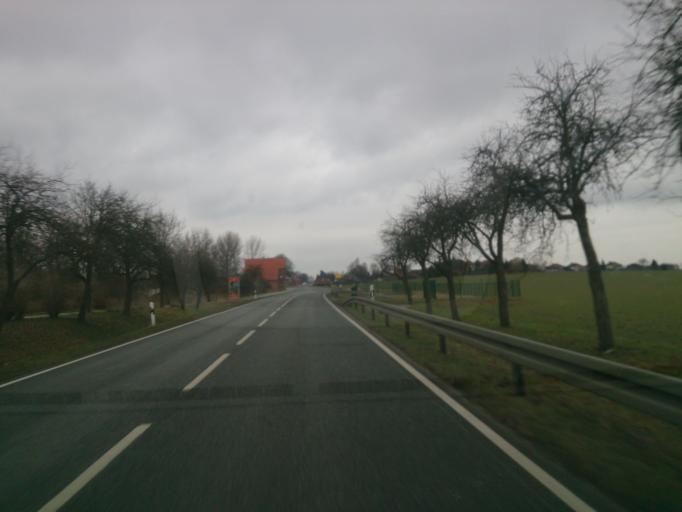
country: DE
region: Mecklenburg-Vorpommern
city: Wackerow
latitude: 53.7197
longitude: 12.9169
